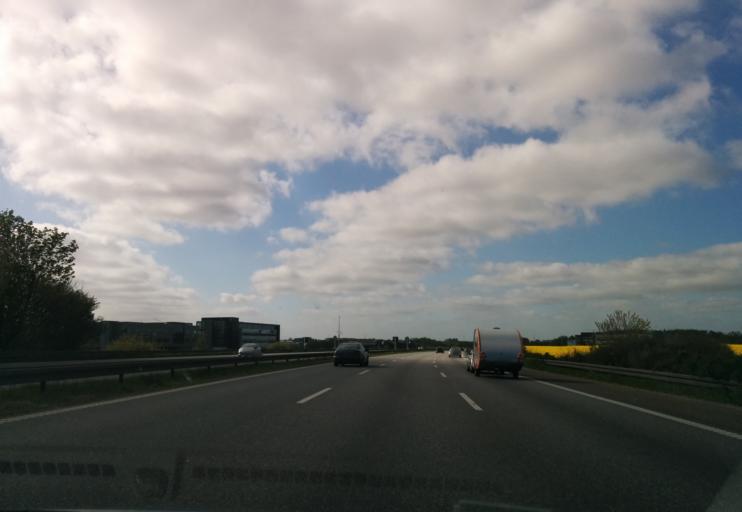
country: DK
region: South Denmark
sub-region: Fredericia Kommune
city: Snoghoj
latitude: 55.5238
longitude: 9.7301
